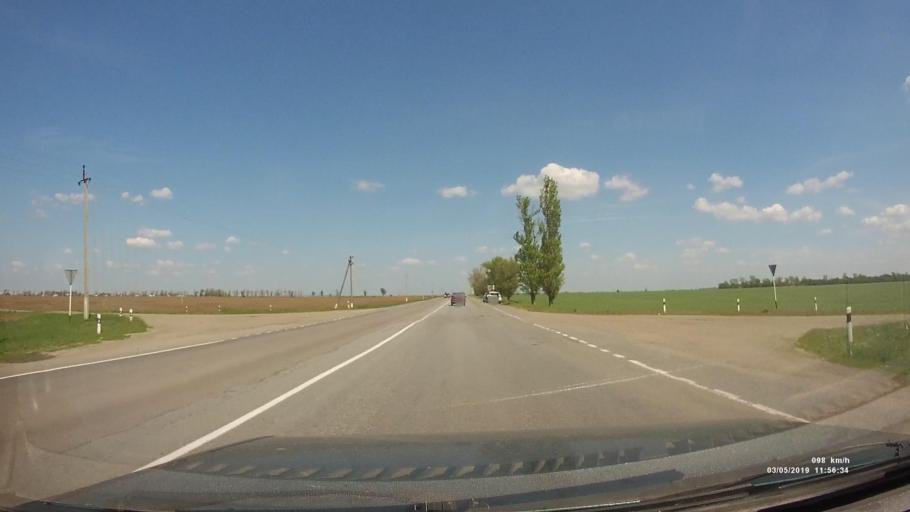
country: RU
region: Rostov
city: Bagayevskaya
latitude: 47.1963
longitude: 40.3022
